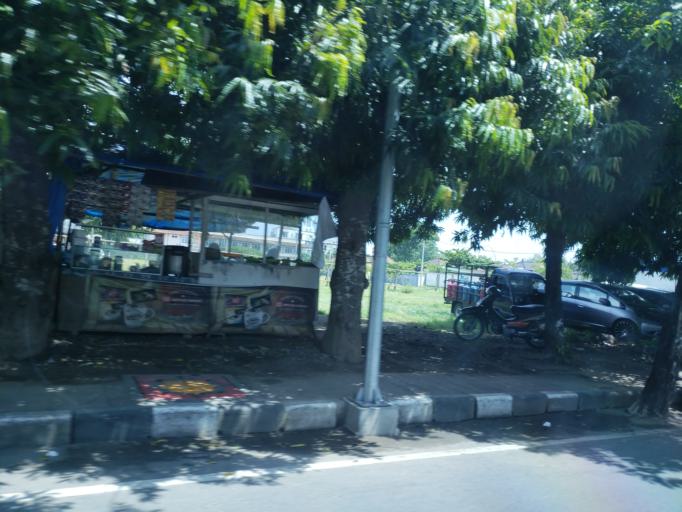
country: ID
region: Bali
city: Kelanabian
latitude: -8.7553
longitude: 115.1774
